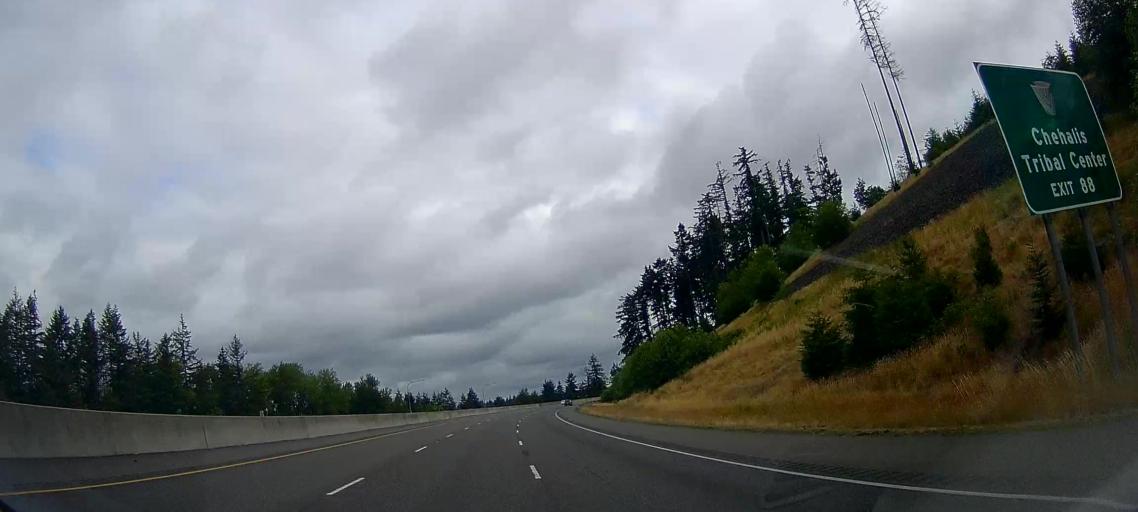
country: US
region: Washington
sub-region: Thurston County
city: Grand Mound
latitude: 46.7947
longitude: -123.0103
